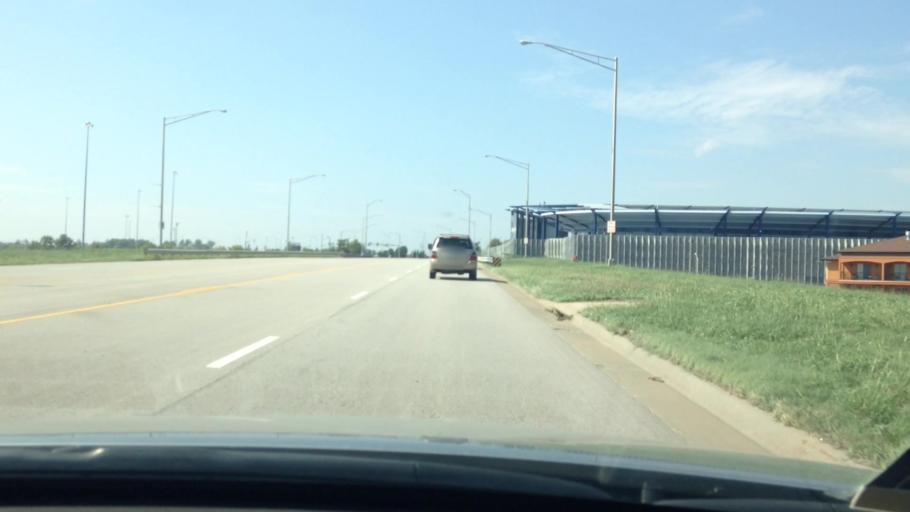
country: US
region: Kansas
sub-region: Wyandotte County
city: Edwardsville
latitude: 39.1188
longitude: -94.8225
